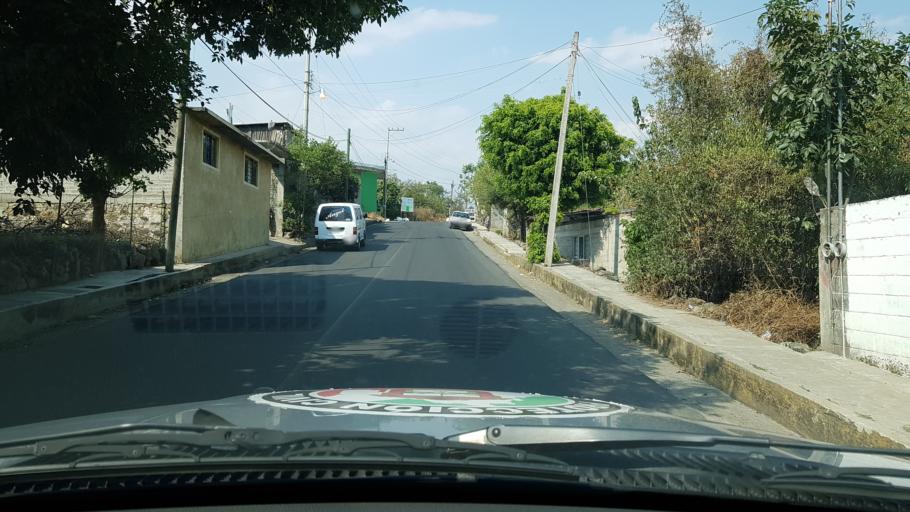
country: MX
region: Mexico
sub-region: Ozumba
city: San Jose Tlacotitlan
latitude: 18.9801
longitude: -98.8107
